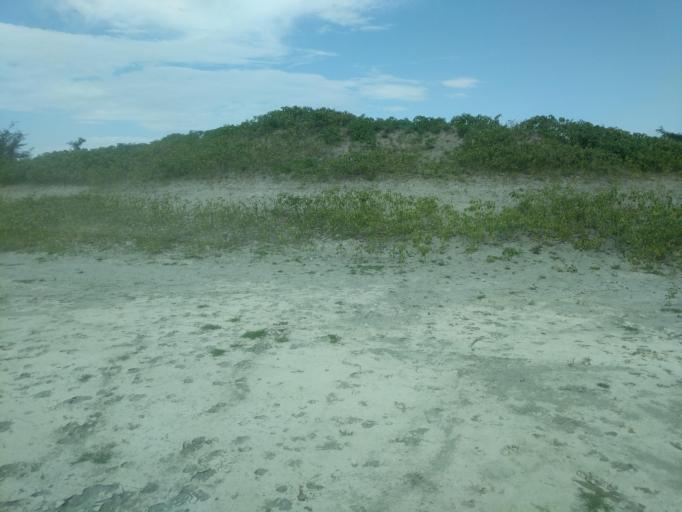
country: ET
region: Oromiya
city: Ziway
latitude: 7.6900
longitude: 38.6469
